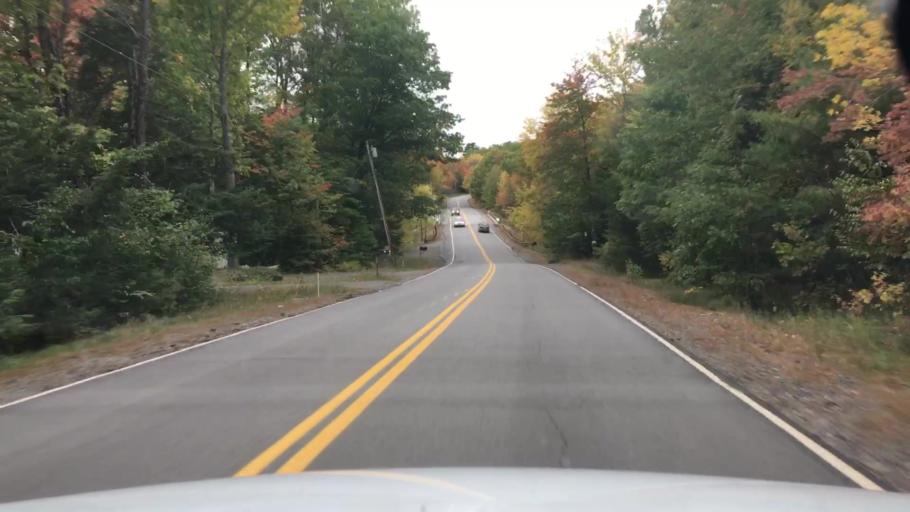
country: US
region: Maine
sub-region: Penobscot County
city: Hudson
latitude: 44.9847
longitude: -68.7910
